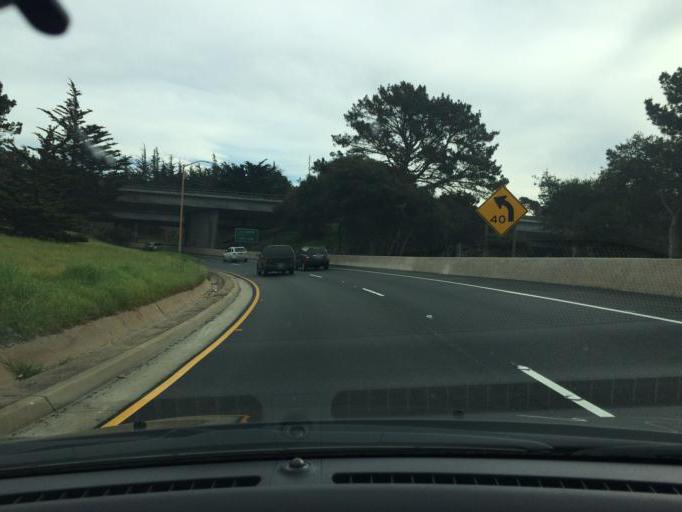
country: US
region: California
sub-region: Monterey County
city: Monterey
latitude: 36.5927
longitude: -121.8810
